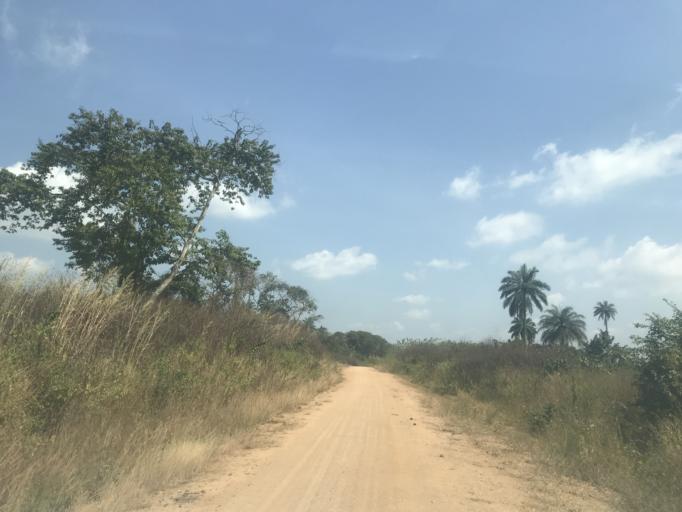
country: NG
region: Osun
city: Otan Ayegbaju
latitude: 7.8943
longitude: 4.8566
